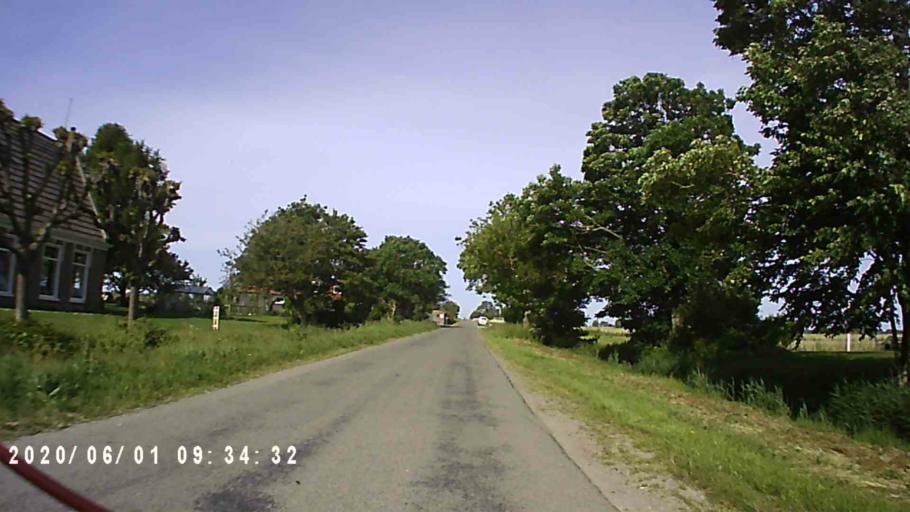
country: NL
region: Friesland
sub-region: Gemeente Leeuwarderadeel
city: Stiens
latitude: 53.2609
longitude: 5.7121
